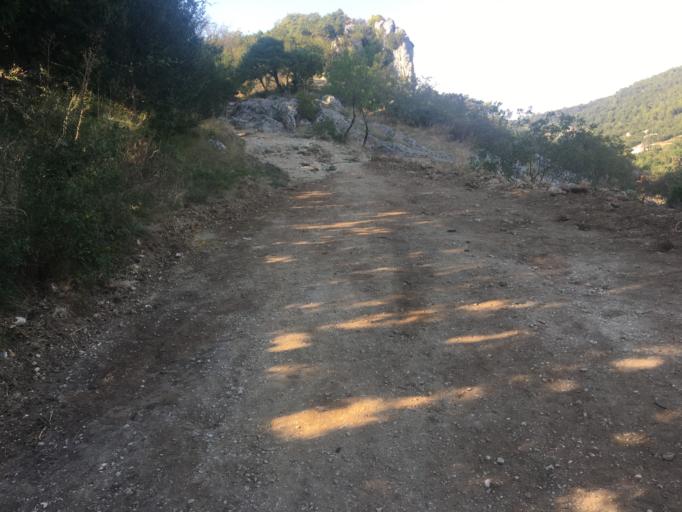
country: FR
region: Languedoc-Roussillon
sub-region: Departement du Gard
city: Saint-Julien-de-Peyrolas
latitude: 44.3049
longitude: 4.5551
